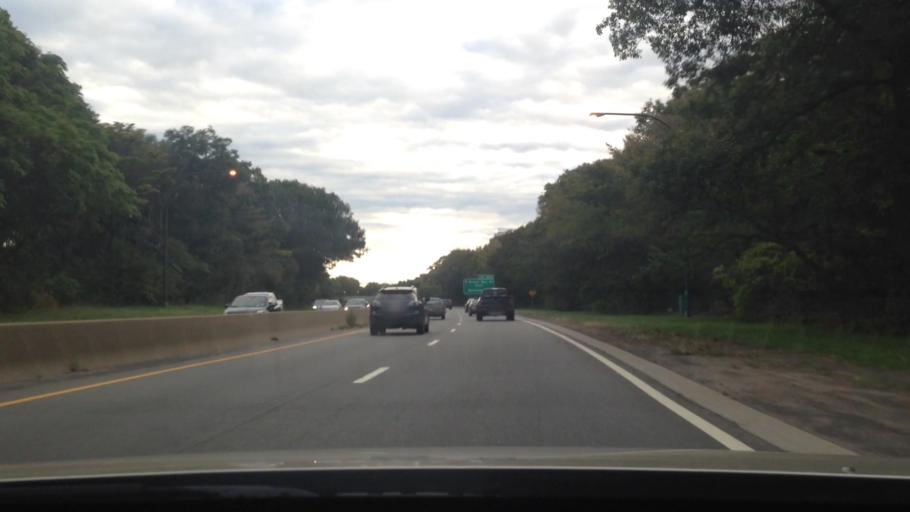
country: US
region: New York
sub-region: Nassau County
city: Hicksville
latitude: 40.7916
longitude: -73.5096
